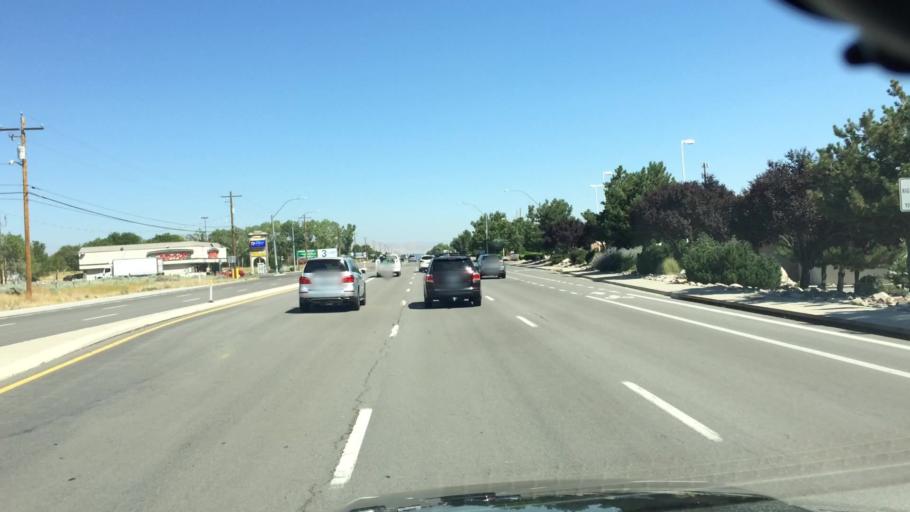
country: US
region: Nevada
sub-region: Washoe County
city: Sparks
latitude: 39.4204
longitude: -119.7575
